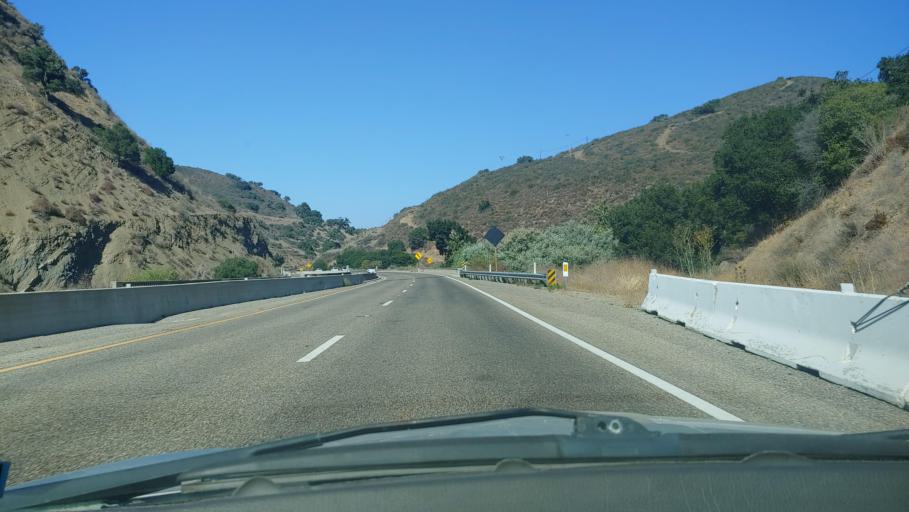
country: US
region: California
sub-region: Santa Barbara County
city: Buellton
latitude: 34.5781
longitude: -120.1937
